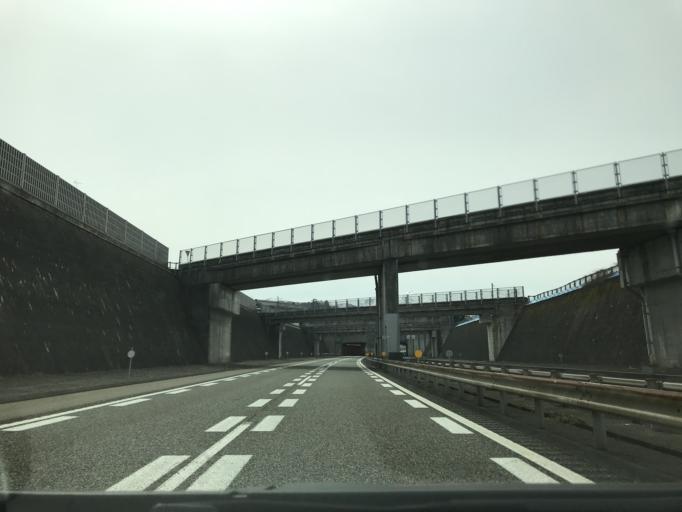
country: JP
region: Niigata
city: Ojiya
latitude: 37.2328
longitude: 138.9758
